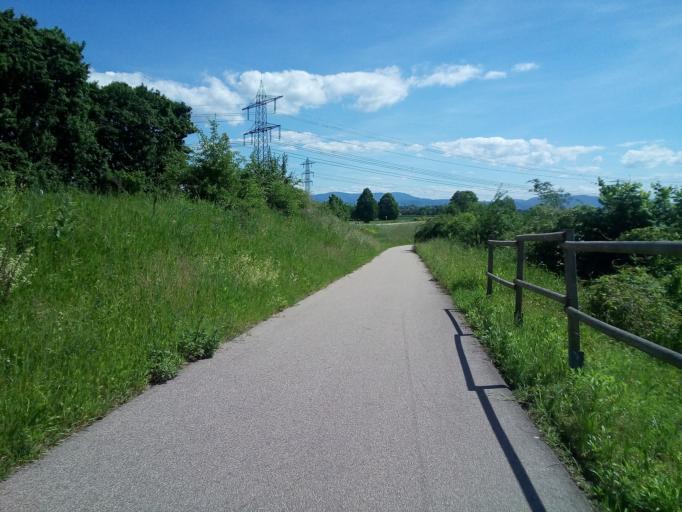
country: DE
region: Baden-Wuerttemberg
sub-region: Freiburg Region
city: Renchen
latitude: 48.6117
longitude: 8.0037
